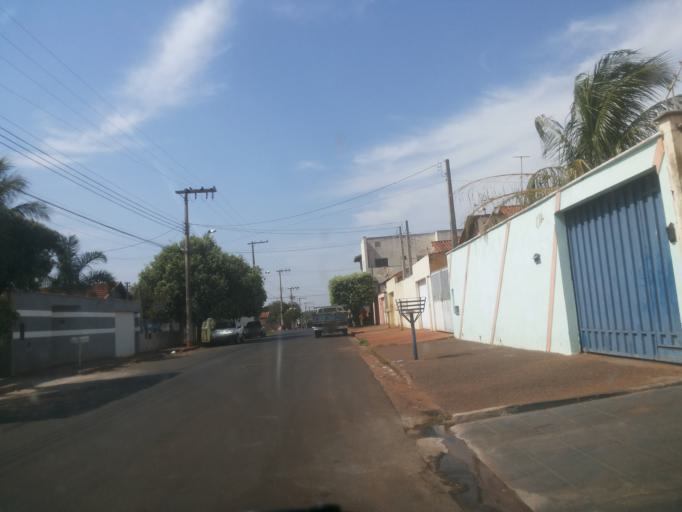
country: BR
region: Minas Gerais
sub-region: Ituiutaba
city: Ituiutaba
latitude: -18.9847
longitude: -49.4841
